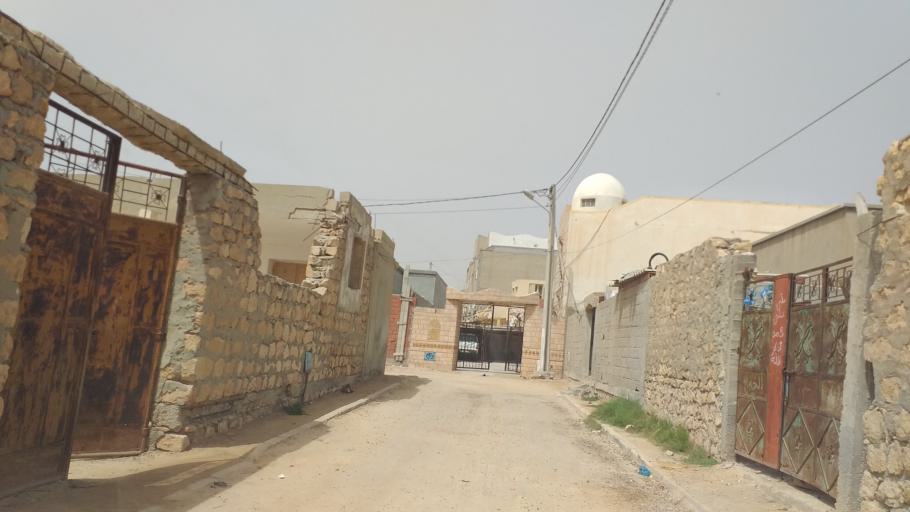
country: TN
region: Qabis
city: Gabes
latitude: 33.9423
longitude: 10.0618
